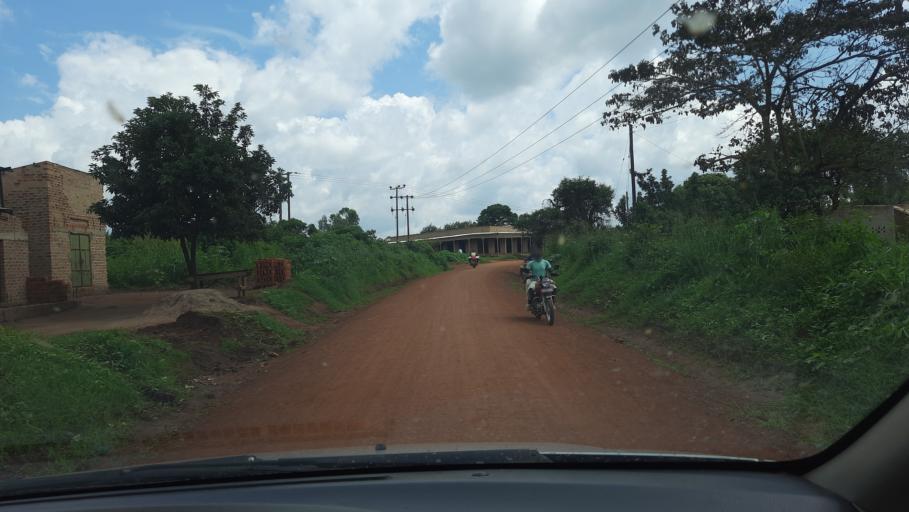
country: UG
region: Western Region
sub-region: Kiryandongo District
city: Kiryandongo
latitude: 1.8138
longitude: 31.9968
